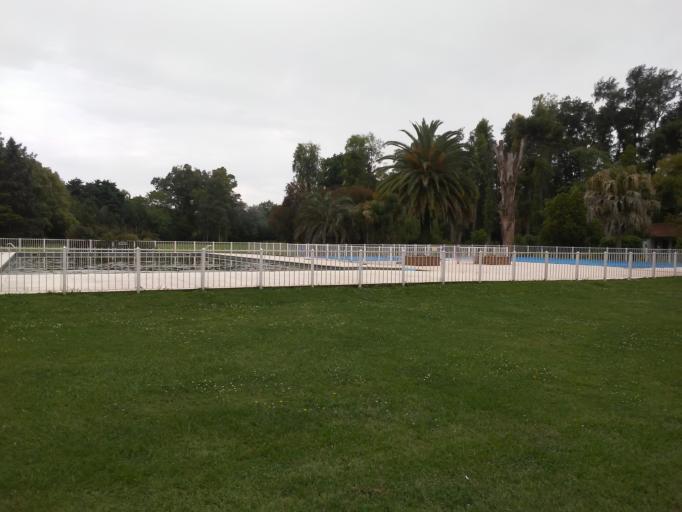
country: AR
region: Buenos Aires
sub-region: Partido de General Rodriguez
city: General Rodriguez
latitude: -34.5966
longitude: -58.9941
